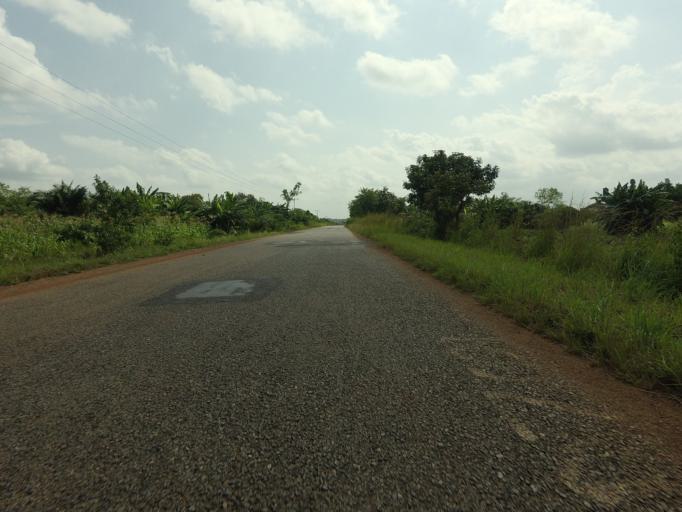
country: TG
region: Maritime
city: Tsevie
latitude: 6.3925
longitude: 0.8189
